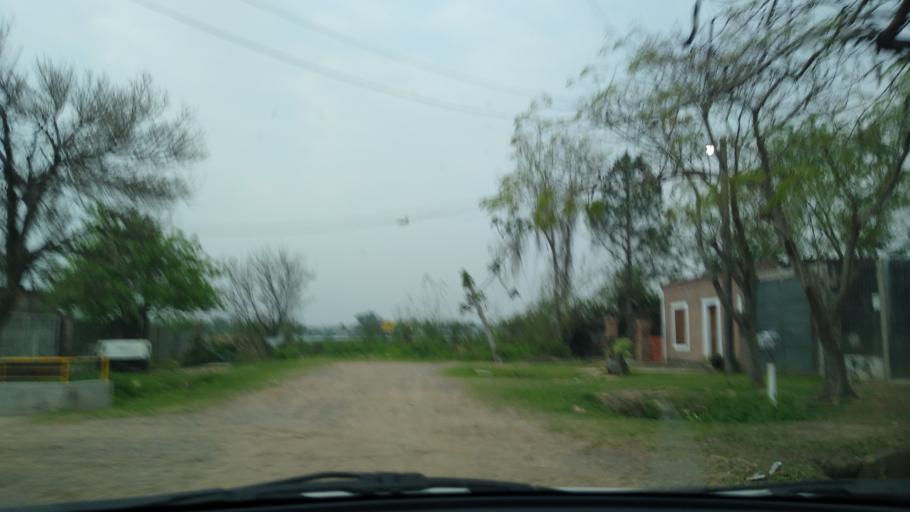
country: AR
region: Chaco
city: Barranqueras
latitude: -27.4804
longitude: -58.9437
